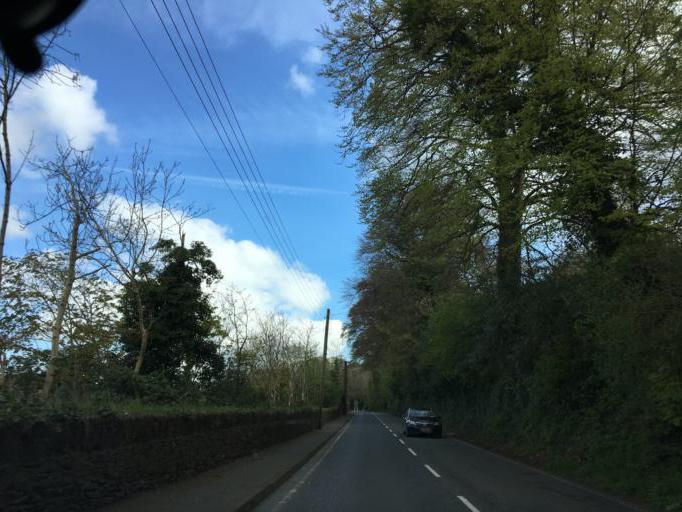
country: IE
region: Leinster
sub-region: Loch Garman
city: New Ross
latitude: 52.3994
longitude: -6.9416
